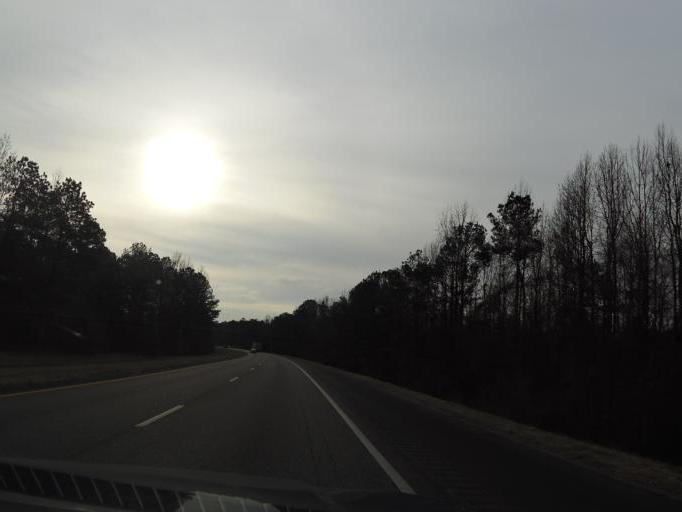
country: US
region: Alabama
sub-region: Autauga County
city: Prattville
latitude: 32.5227
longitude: -86.4407
